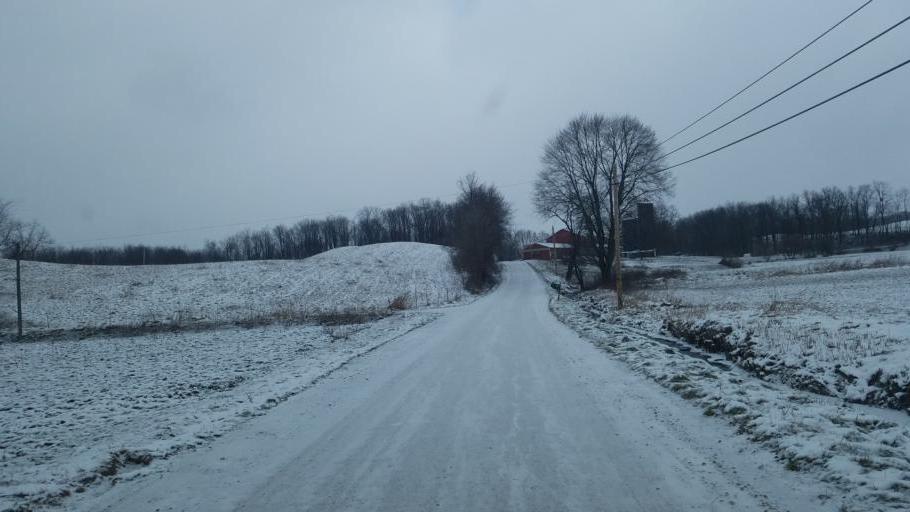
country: US
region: Pennsylvania
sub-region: Venango County
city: Sugarcreek
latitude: 41.4550
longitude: -79.9636
